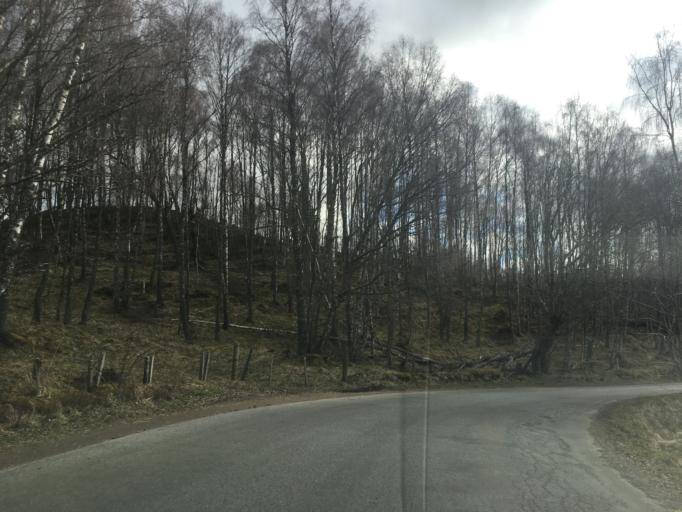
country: GB
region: Scotland
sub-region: Highland
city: Aviemore
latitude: 57.1702
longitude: -3.8256
